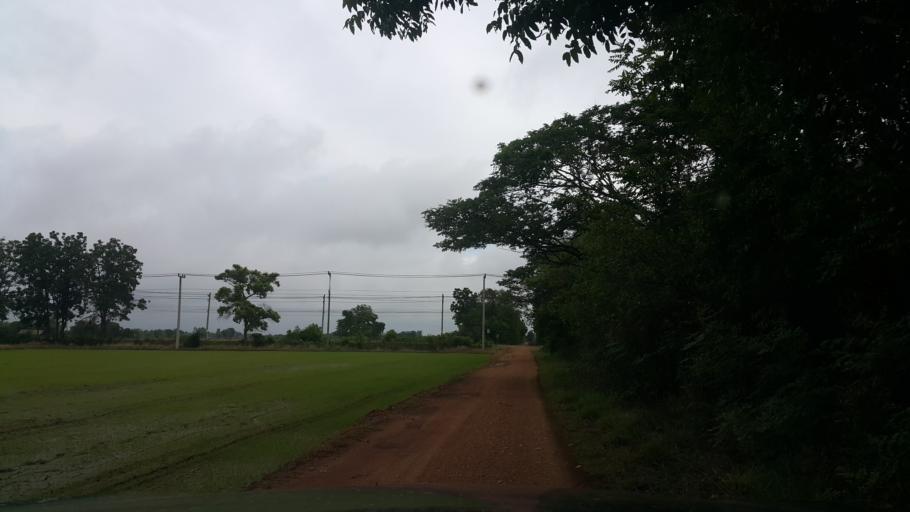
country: TH
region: Sukhothai
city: Sawankhalok
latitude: 17.3089
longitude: 99.7143
